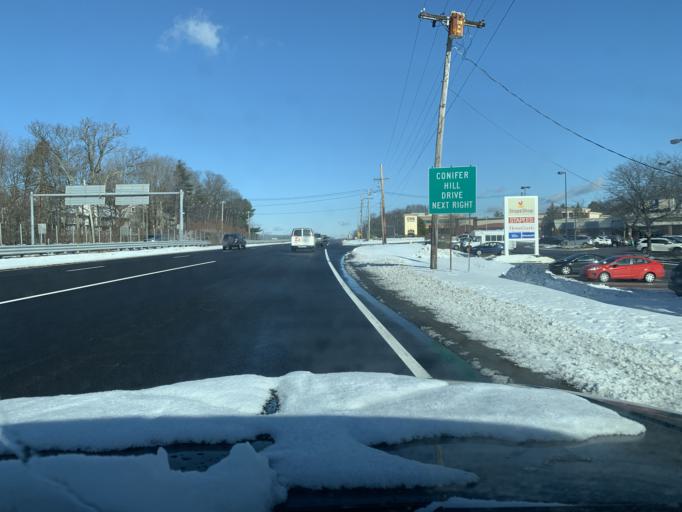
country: US
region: Massachusetts
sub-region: Essex County
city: Danvers
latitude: 42.5855
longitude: -70.9663
